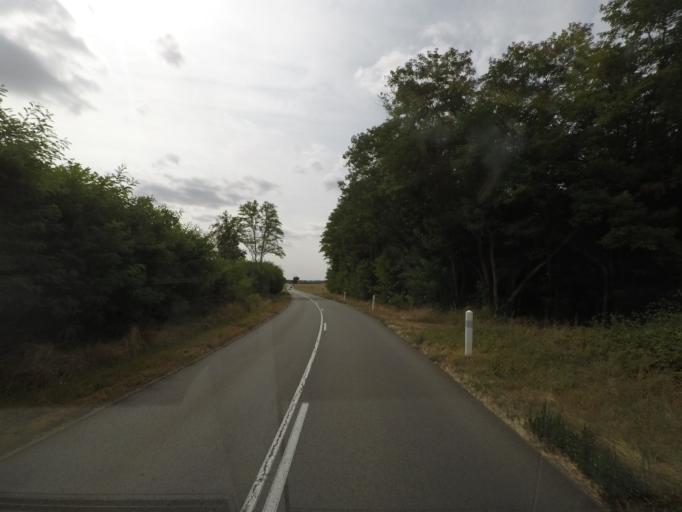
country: FR
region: Poitou-Charentes
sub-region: Departement de la Charente
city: Nanteuil-en-Vallee
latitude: 46.0187
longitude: 0.2916
